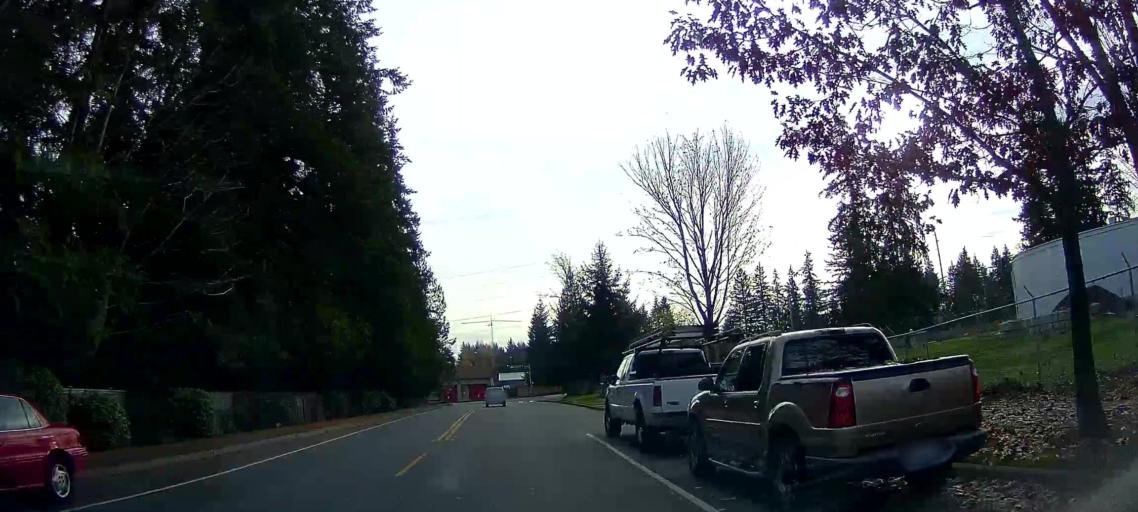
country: US
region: Washington
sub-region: King County
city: Kenmore
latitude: 47.7926
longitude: -122.2384
